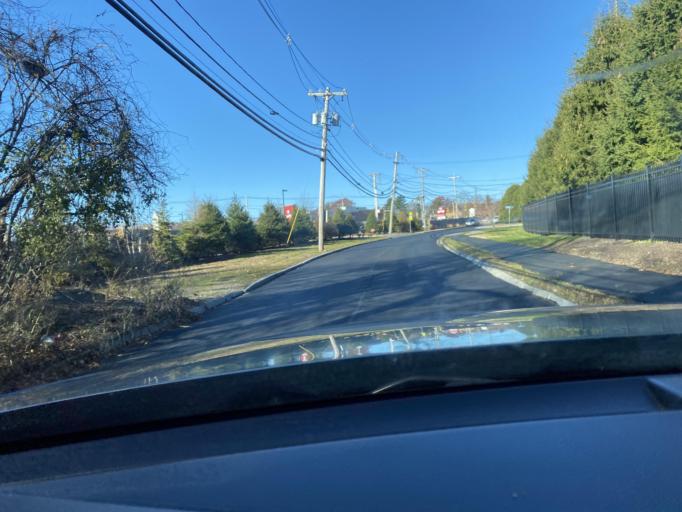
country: US
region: Massachusetts
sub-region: Norfolk County
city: Norwood
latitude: 42.1628
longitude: -71.1978
